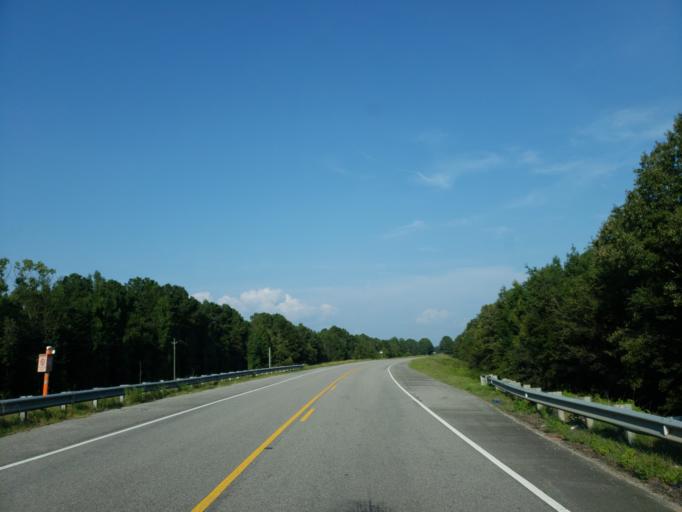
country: US
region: Alabama
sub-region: Sumter County
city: Livingston
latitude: 32.6971
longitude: -88.1092
